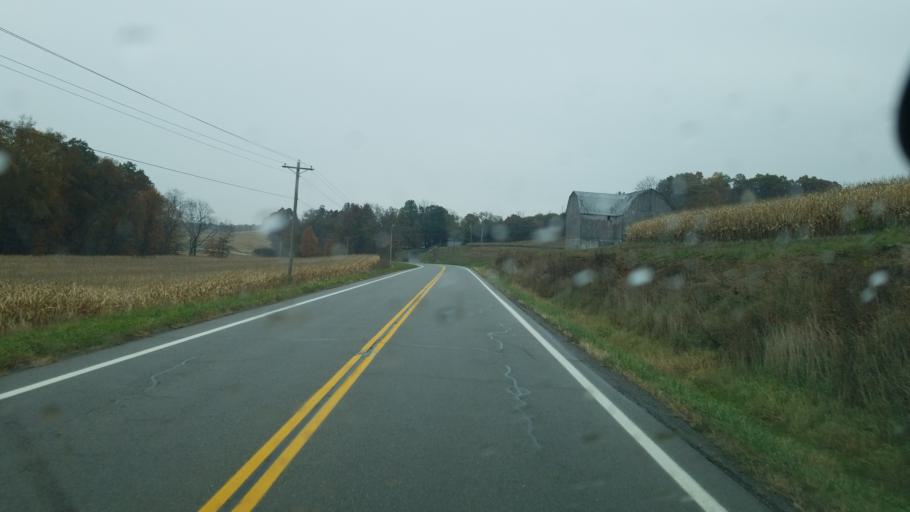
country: US
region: Ohio
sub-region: Coshocton County
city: Coshocton
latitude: 40.3951
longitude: -81.8702
